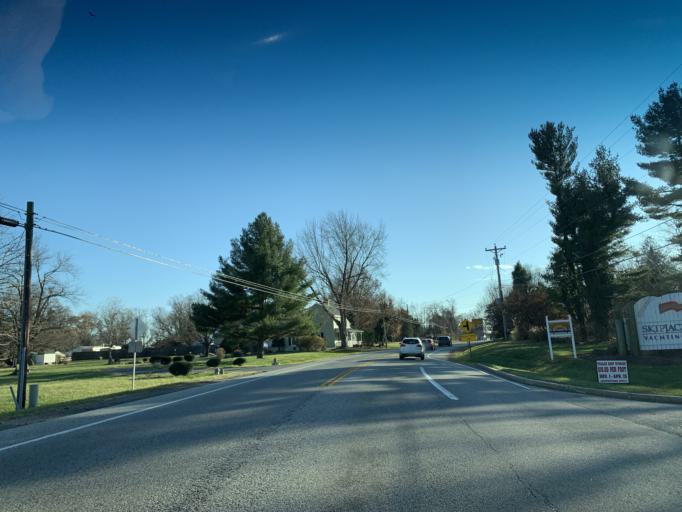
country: US
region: Delaware
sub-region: New Castle County
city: Middletown
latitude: 39.3700
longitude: -75.8830
